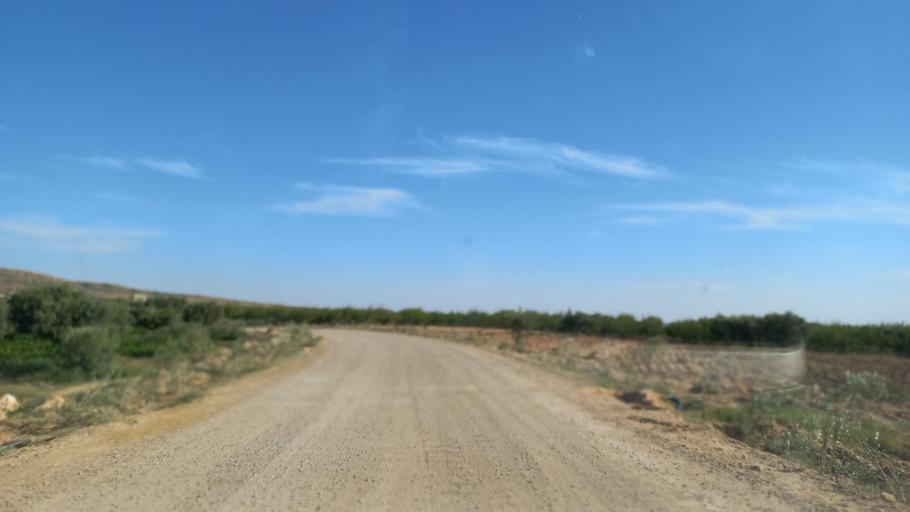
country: TN
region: Al Qasrayn
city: Sbiba
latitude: 35.2979
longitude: 9.0971
